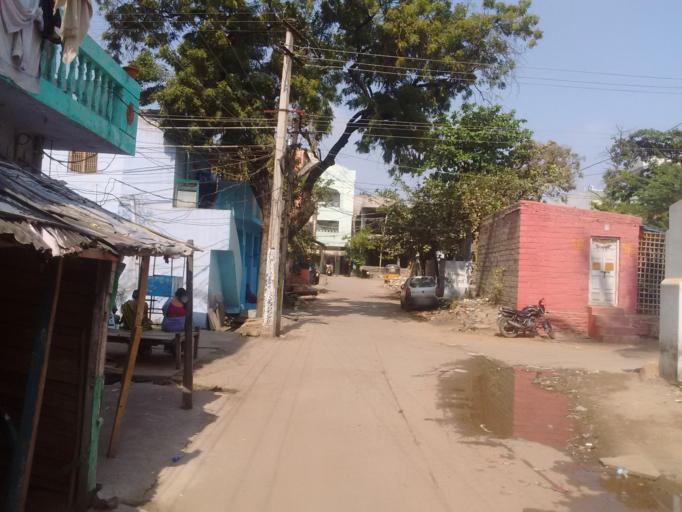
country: IN
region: Telangana
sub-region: Mahbubnagar
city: Alampur
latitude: 15.8126
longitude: 78.0412
